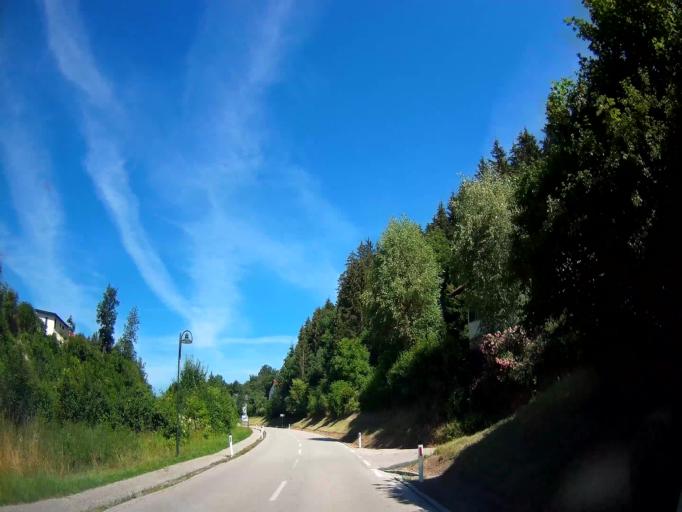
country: AT
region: Carinthia
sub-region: Politischer Bezirk Sankt Veit an der Glan
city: St. Georgen am Laengsee
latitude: 46.7640
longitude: 14.4237
